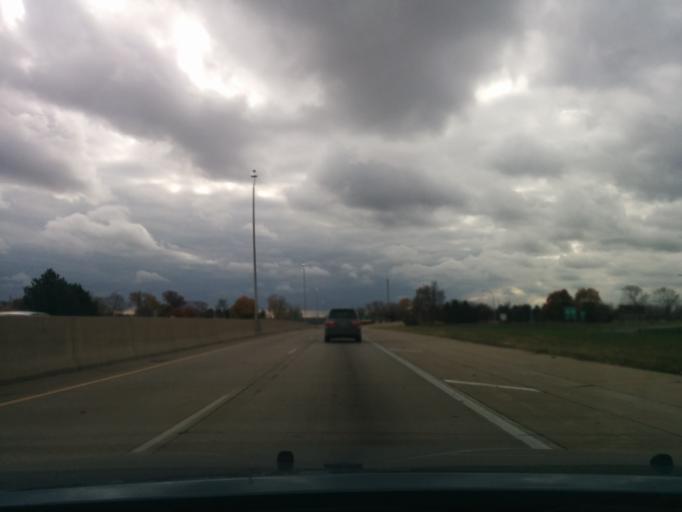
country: US
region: Michigan
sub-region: Wayne County
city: Dearborn
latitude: 42.3139
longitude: -83.2151
